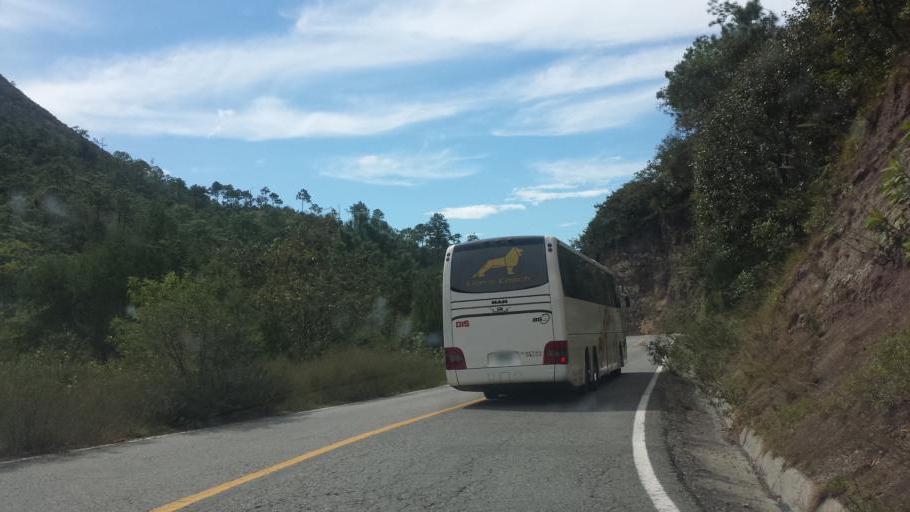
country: MX
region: Oaxaca
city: San Francisco Sola
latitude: 16.4490
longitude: -97.0316
